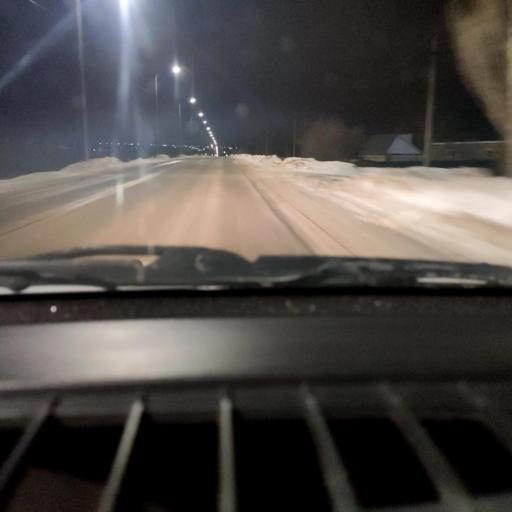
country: RU
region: Bashkortostan
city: Kabakovo
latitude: 54.5801
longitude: 56.2854
